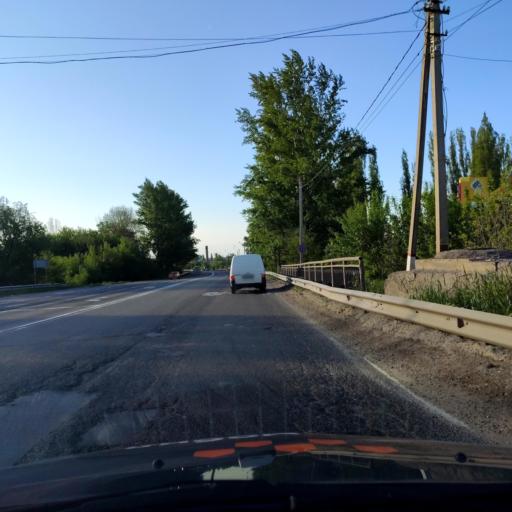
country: RU
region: Lipetsk
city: Yelets
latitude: 52.5998
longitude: 38.4733
